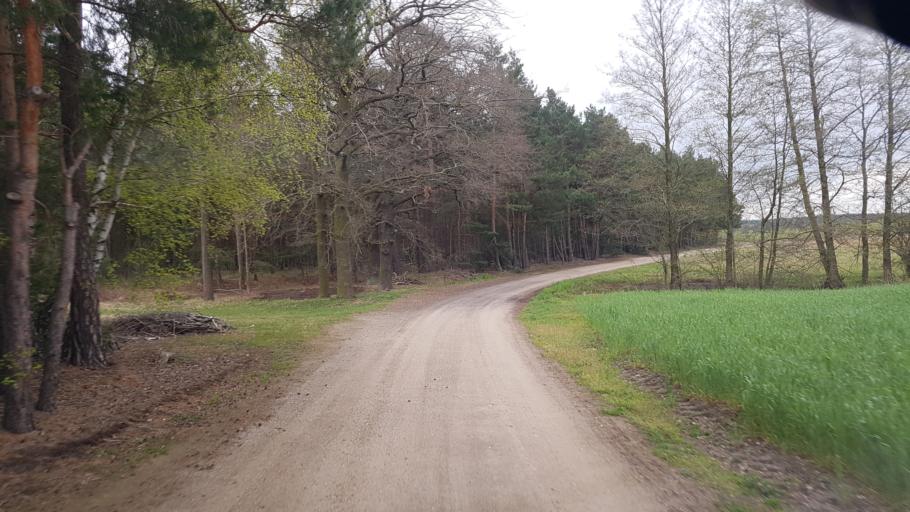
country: DE
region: Brandenburg
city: Altdobern
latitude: 51.6827
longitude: 14.0552
